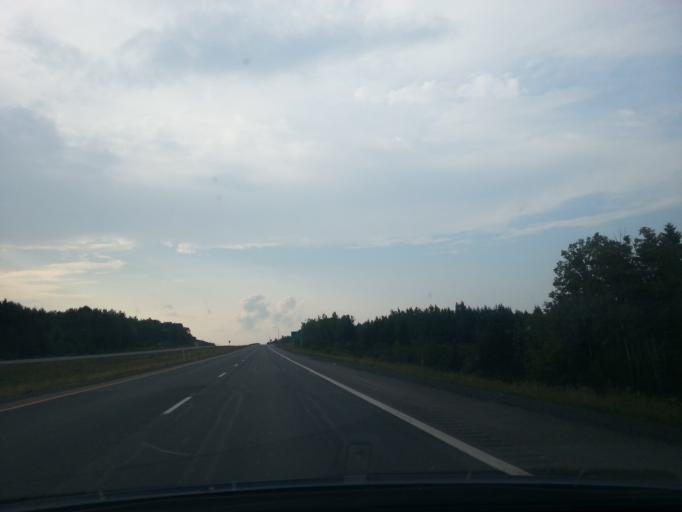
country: CA
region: New Brunswick
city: Harrison Brook
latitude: 47.2554
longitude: -67.9845
